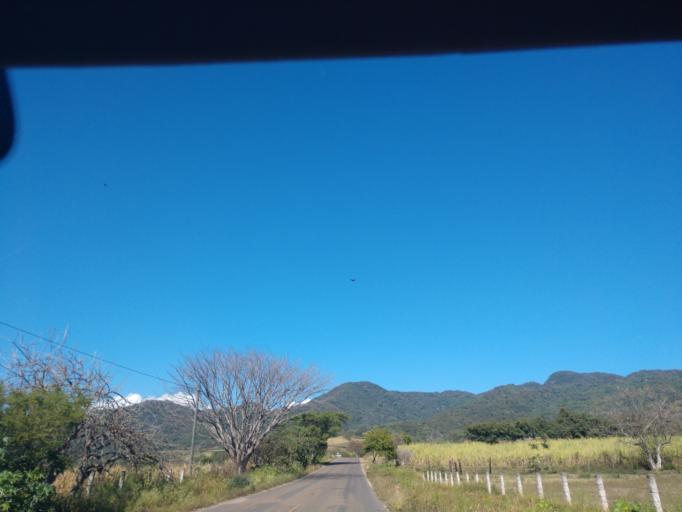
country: MX
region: Nayarit
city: Compostela
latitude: 21.2769
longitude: -104.8801
